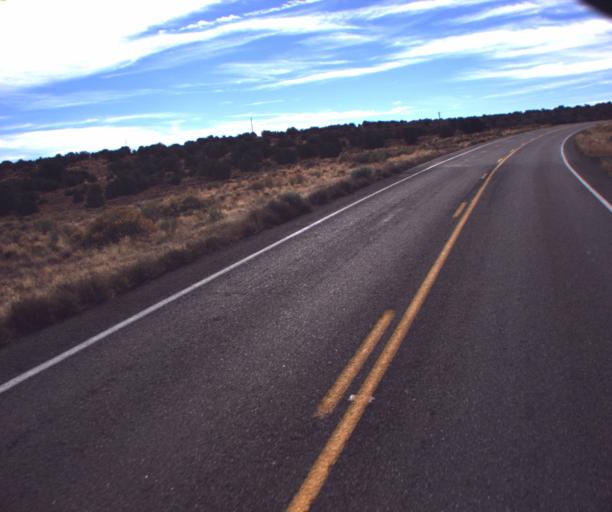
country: US
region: Arizona
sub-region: Coconino County
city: Kaibito
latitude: 36.6831
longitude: -111.2551
